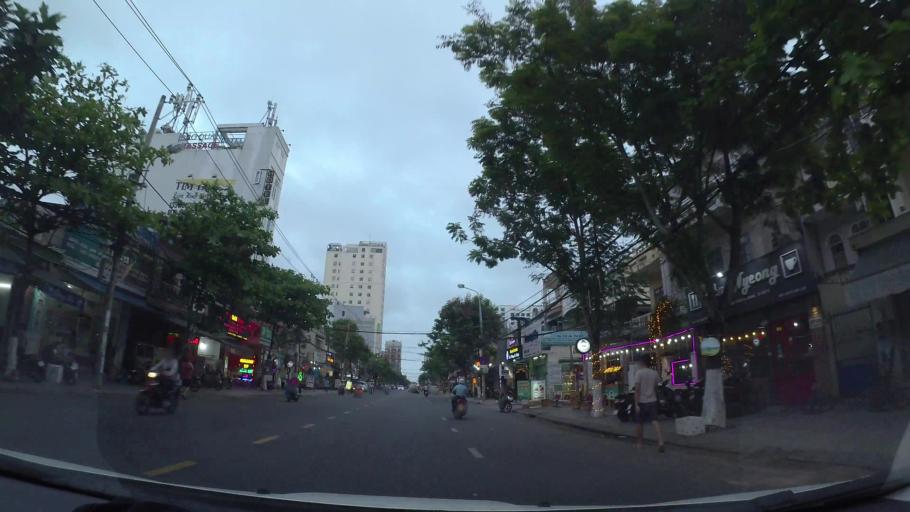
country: VN
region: Da Nang
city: Son Tra
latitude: 16.0545
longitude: 108.2403
